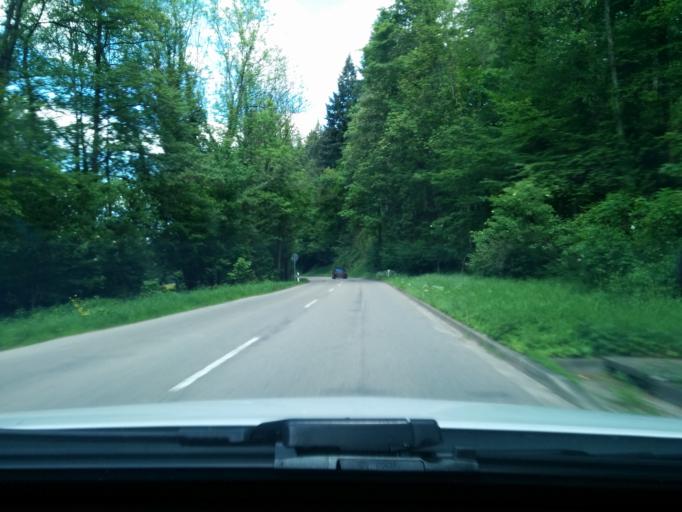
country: DE
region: Baden-Wuerttemberg
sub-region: Freiburg Region
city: Horben
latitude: 47.9422
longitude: 7.8677
